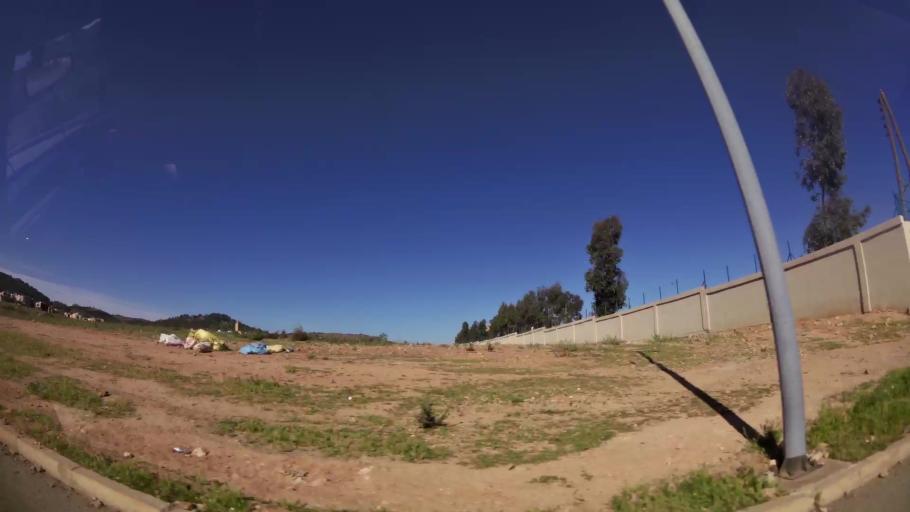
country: MA
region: Oriental
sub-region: Oujda-Angad
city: Oujda
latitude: 34.6521
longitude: -1.8883
